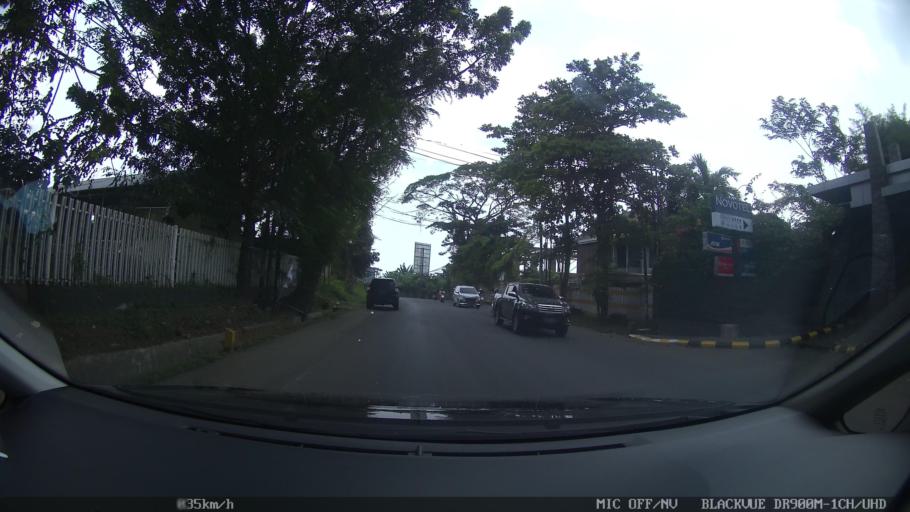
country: ID
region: Lampung
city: Bandarlampung
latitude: -5.4406
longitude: 105.2897
